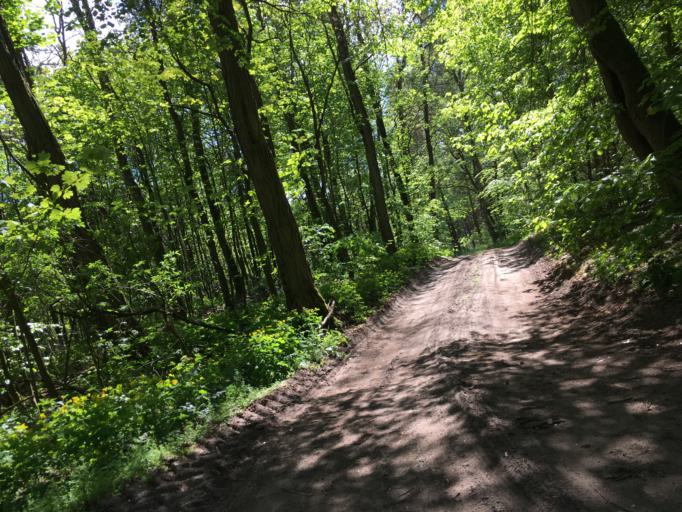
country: DE
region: Brandenburg
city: Rudnitz
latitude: 52.7105
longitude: 13.6601
